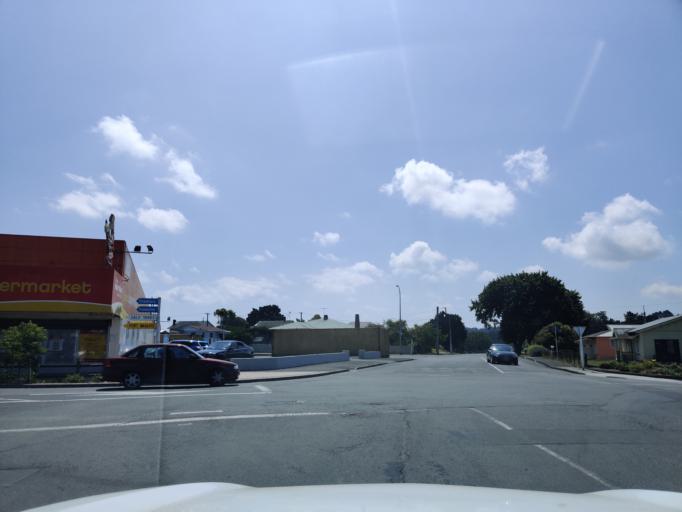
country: NZ
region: Auckland
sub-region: Auckland
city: Pukekohe East
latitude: -37.2573
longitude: 174.9473
